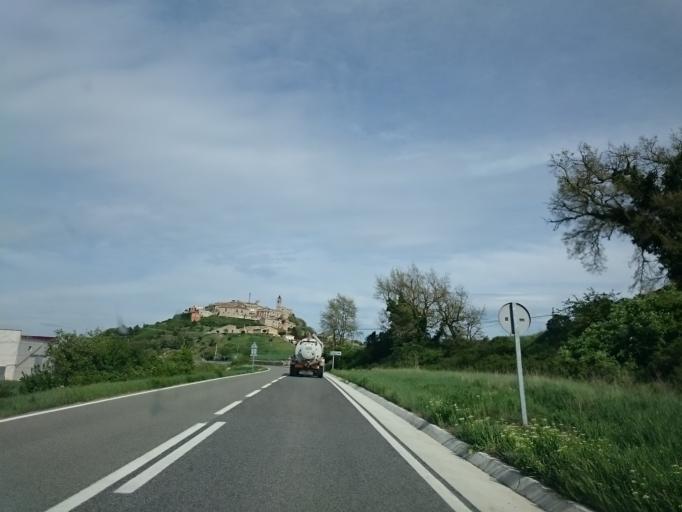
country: ES
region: Catalonia
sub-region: Provincia de Tarragona
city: Santa Coloma de Queralt
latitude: 41.5528
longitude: 1.4122
